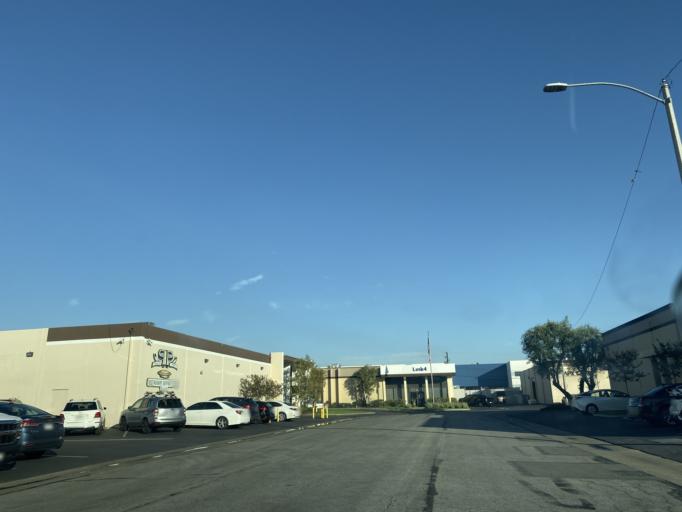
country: US
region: California
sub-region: Orange County
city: Fullerton
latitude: 33.8625
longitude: -117.9170
